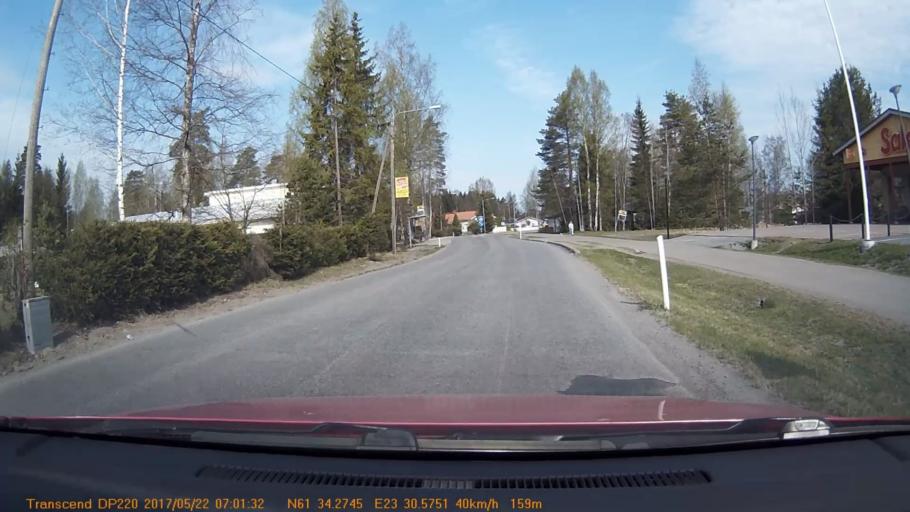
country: FI
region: Pirkanmaa
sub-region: Tampere
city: Yloejaervi
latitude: 61.5713
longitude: 23.5096
